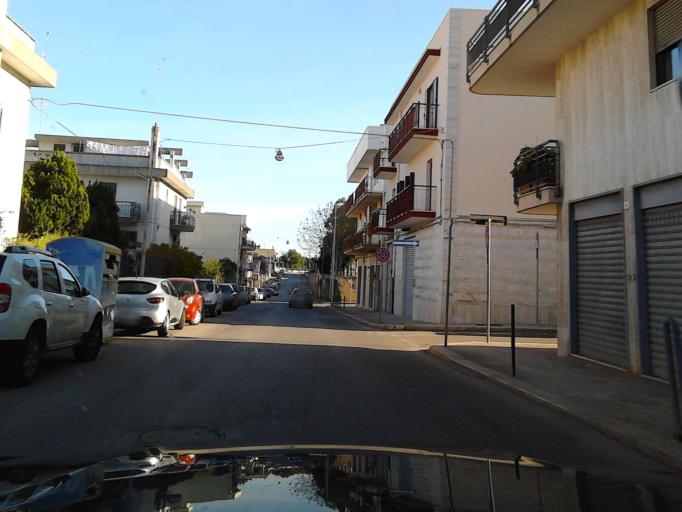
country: IT
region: Apulia
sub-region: Provincia di Bari
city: Mola di Bari
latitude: 41.0557
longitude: 17.0831
